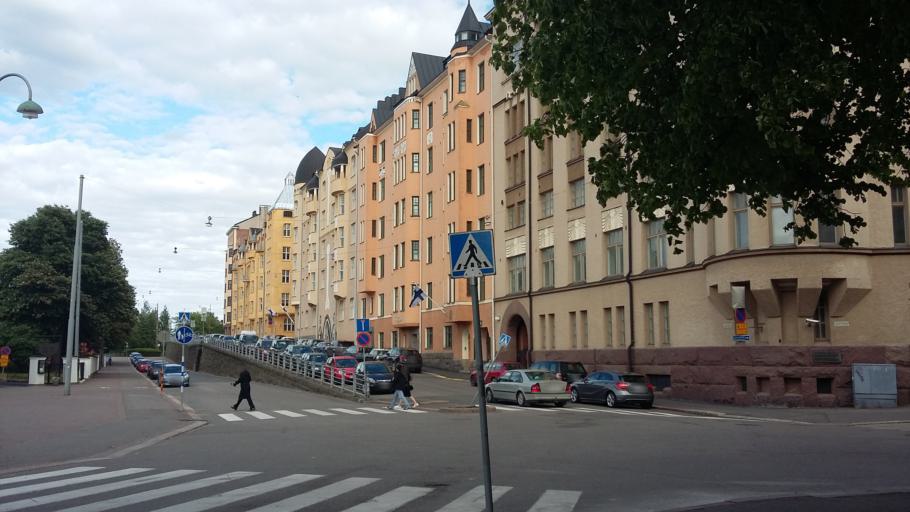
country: FI
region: Uusimaa
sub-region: Helsinki
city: Helsinki
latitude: 60.1688
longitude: 24.9633
